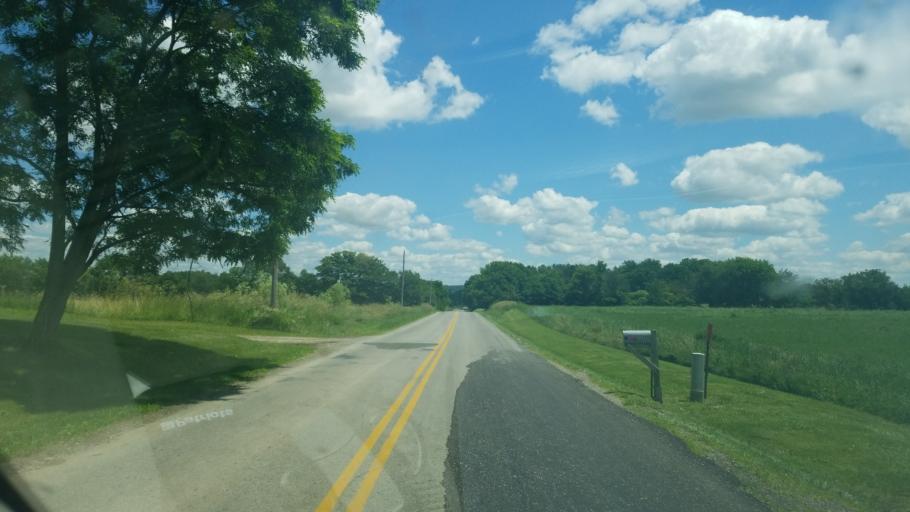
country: US
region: Ohio
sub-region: Ashland County
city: Ashland
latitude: 40.9532
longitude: -82.3860
